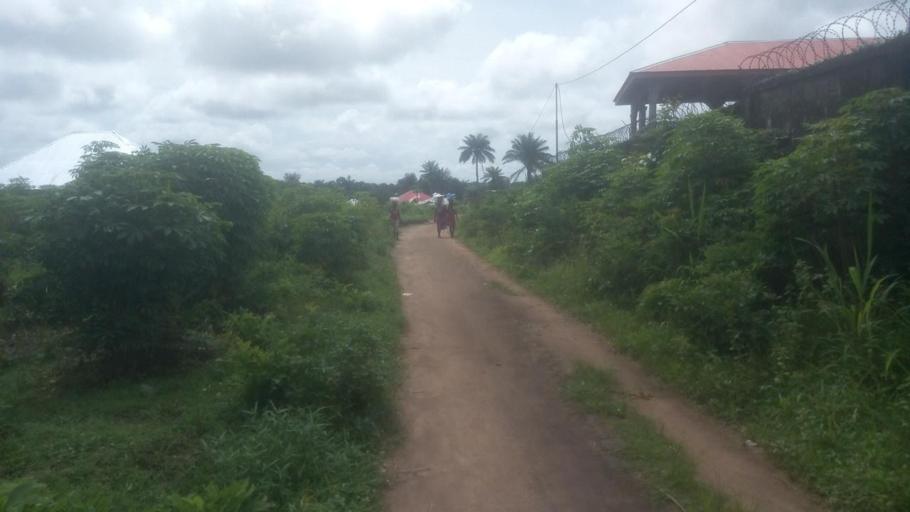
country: SL
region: Northern Province
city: Masoyila
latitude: 8.5904
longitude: -13.1872
